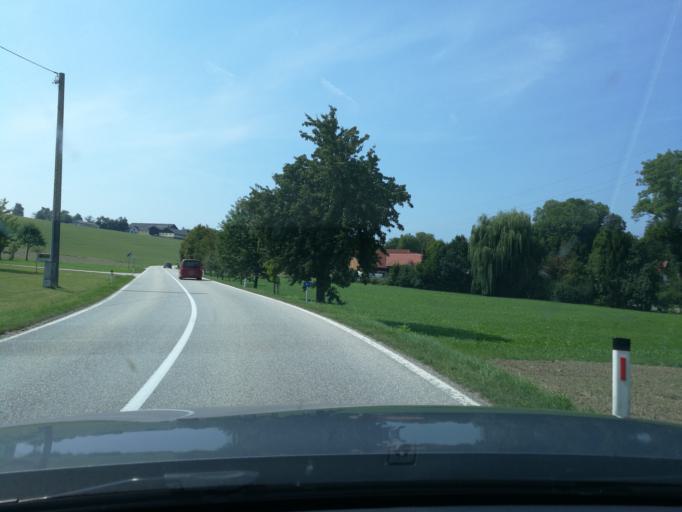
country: AT
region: Upper Austria
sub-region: Politischer Bezirk Grieskirchen
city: Grieskirchen
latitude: 48.3504
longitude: 13.7365
